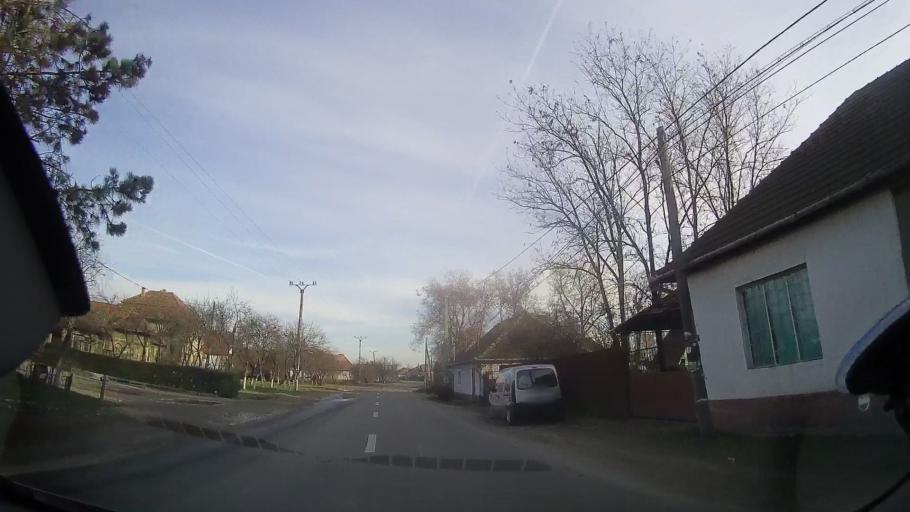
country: RO
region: Bihor
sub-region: Comuna Tileagd
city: Tileagd
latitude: 47.0692
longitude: 22.2007
